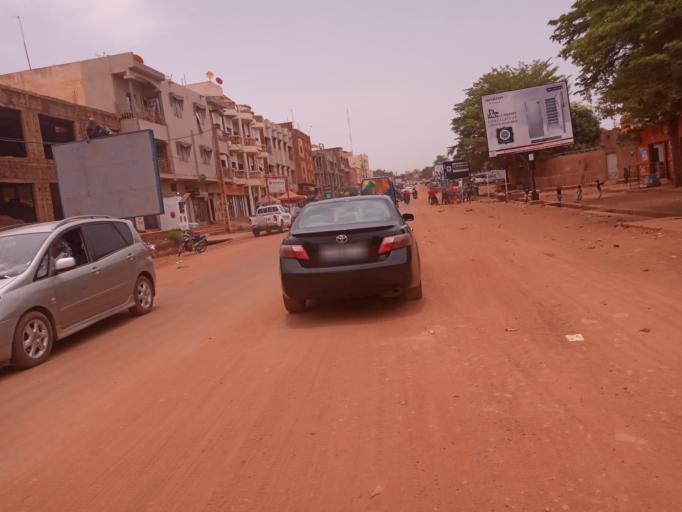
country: ML
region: Bamako
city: Bamako
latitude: 12.5757
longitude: -8.0103
